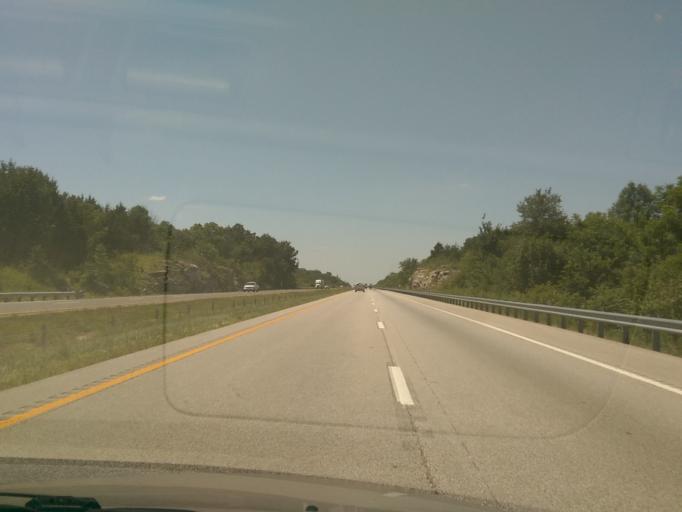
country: US
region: Missouri
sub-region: Cooper County
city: Boonville
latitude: 38.9338
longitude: -92.9566
